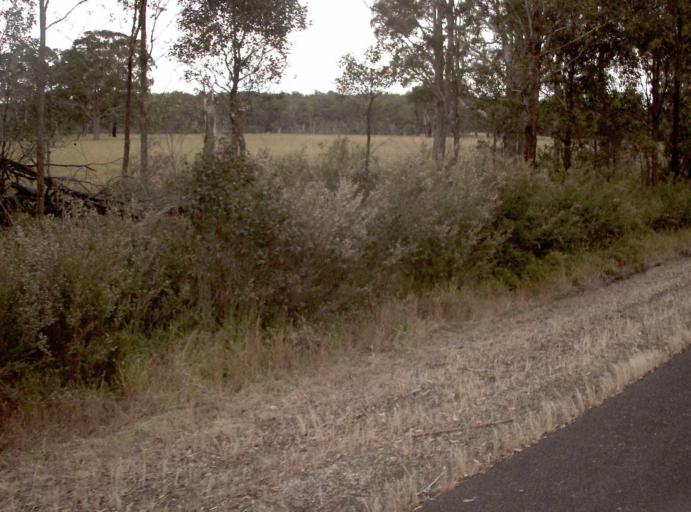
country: AU
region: Victoria
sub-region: Wellington
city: Sale
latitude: -38.4695
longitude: 146.9298
